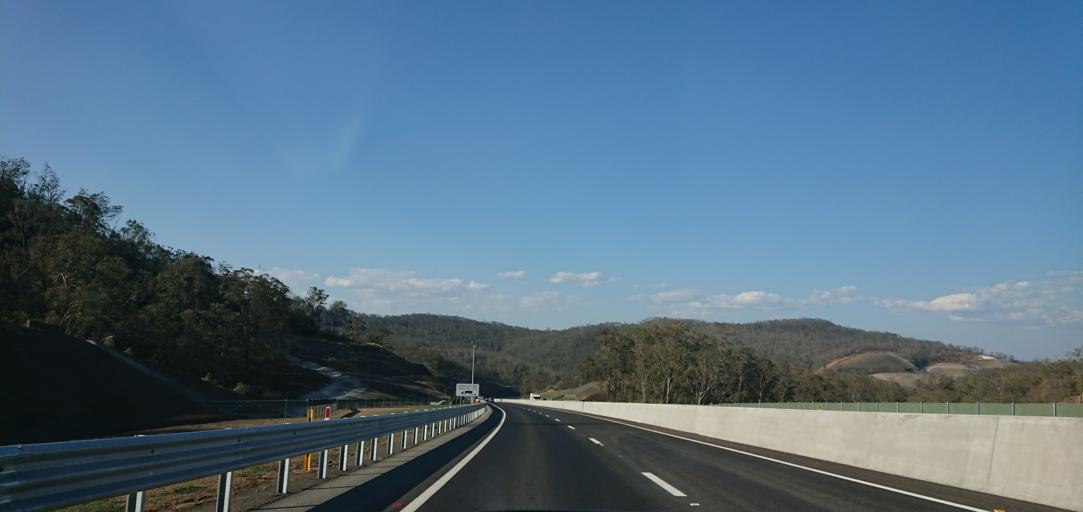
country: AU
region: Queensland
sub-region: Toowoomba
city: Wilsonton Heights
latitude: -27.5067
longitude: 151.9706
